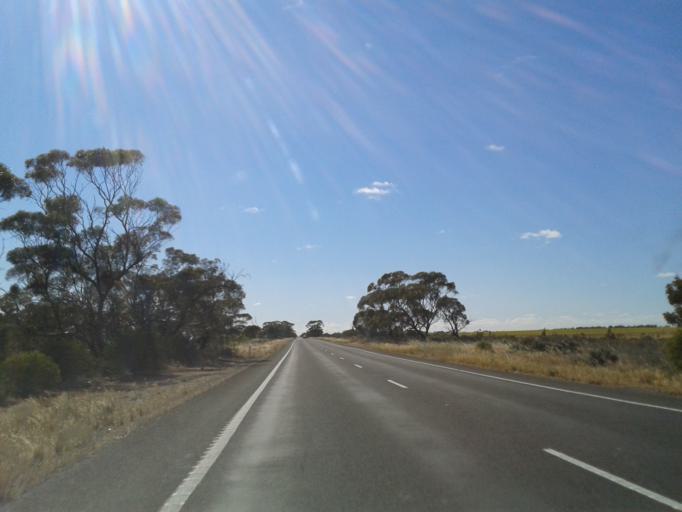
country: AU
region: South Australia
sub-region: Renmark Paringa
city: Renmark
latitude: -34.2756
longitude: 141.3112
